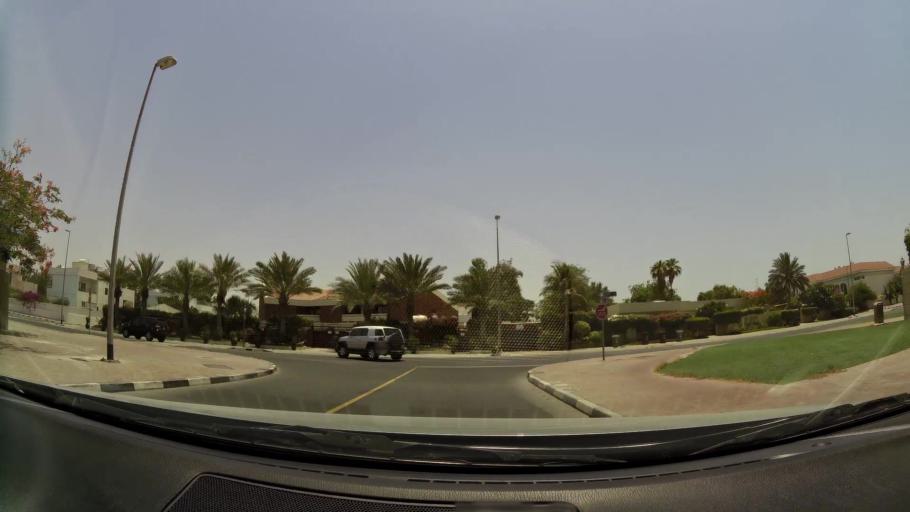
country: AE
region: Dubai
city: Dubai
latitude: 25.2126
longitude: 55.2543
